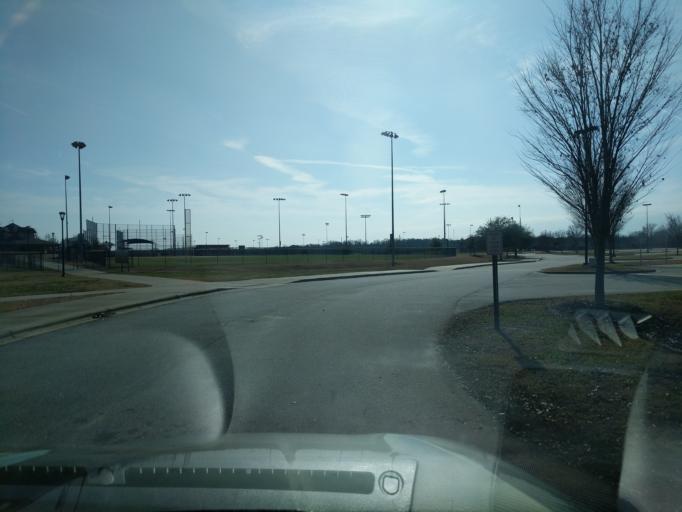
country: US
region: South Carolina
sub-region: Spartanburg County
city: Duncan
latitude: 34.8734
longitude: -82.1058
